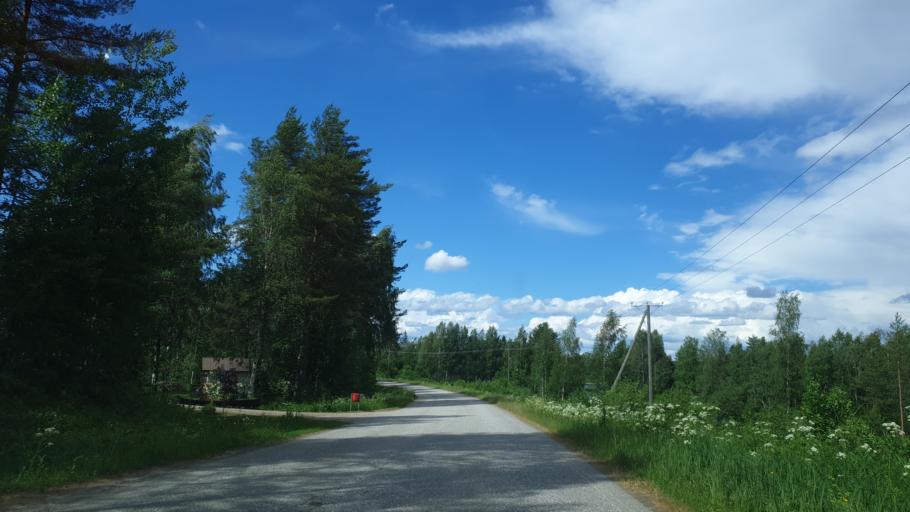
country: FI
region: Northern Savo
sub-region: Koillis-Savo
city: Kaavi
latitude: 62.9980
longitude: 28.7158
